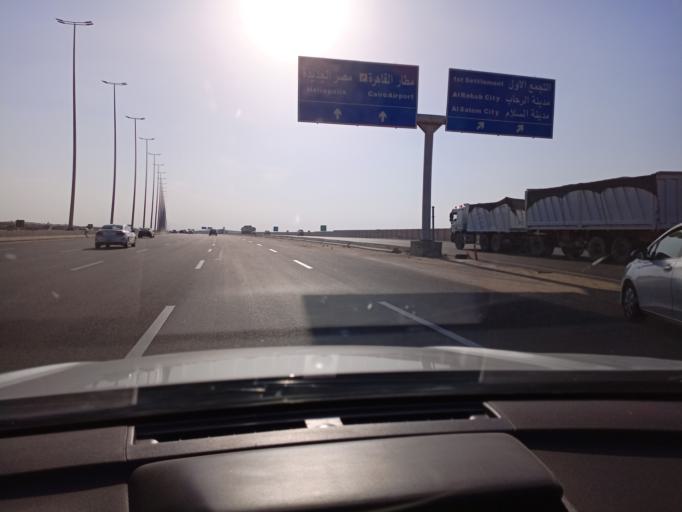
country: EG
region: Muhafazat al Qalyubiyah
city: Al Khankah
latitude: 30.0898
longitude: 31.4630
